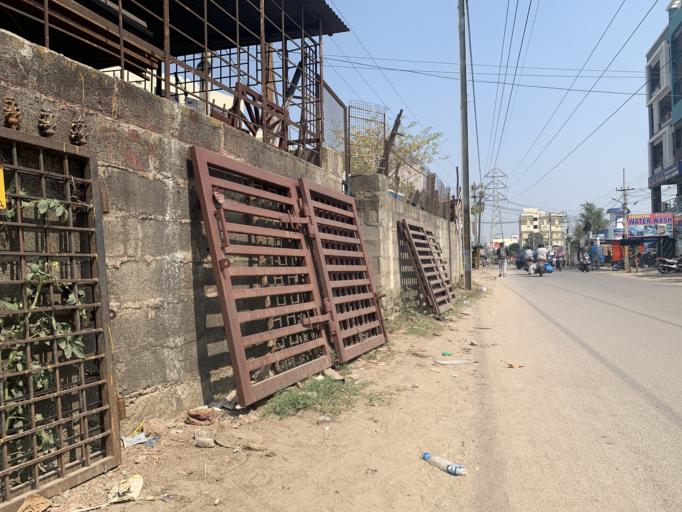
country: IN
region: Telangana
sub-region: Rangareddi
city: Kukatpalli
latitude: 17.4956
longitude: 78.4202
